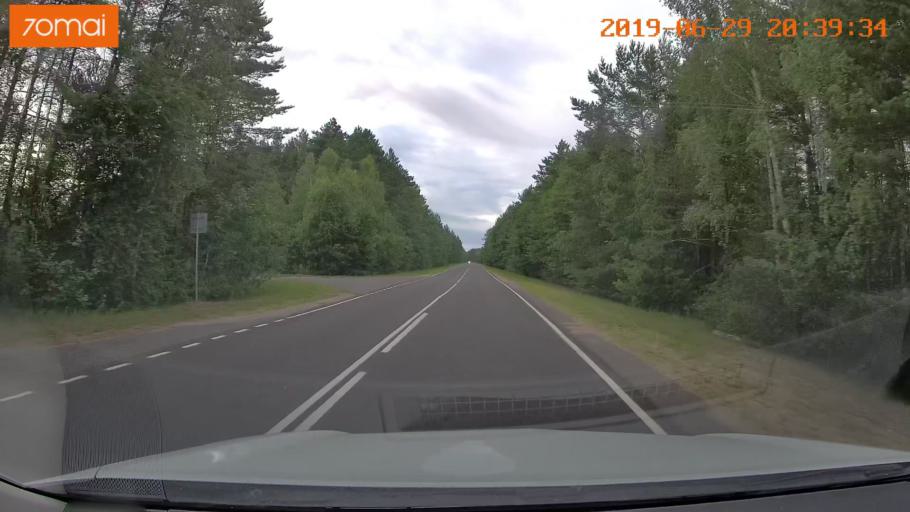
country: BY
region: Brest
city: Hantsavichy
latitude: 52.5642
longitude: 26.3616
